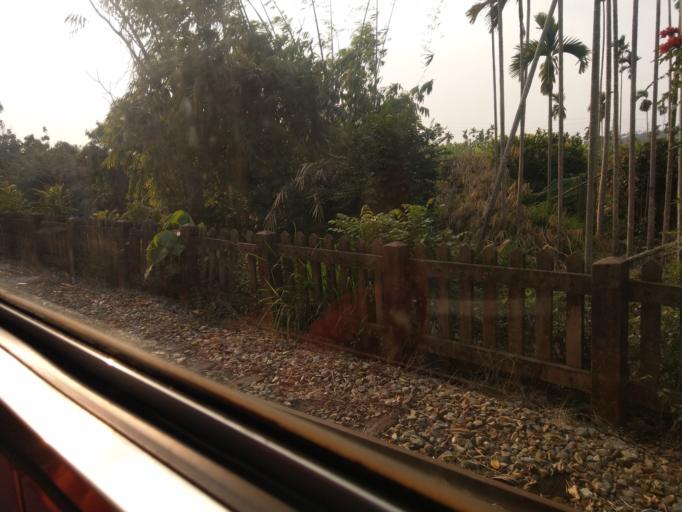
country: TW
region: Taiwan
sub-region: Chiayi
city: Jiayi Shi
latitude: 23.5039
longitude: 120.5309
